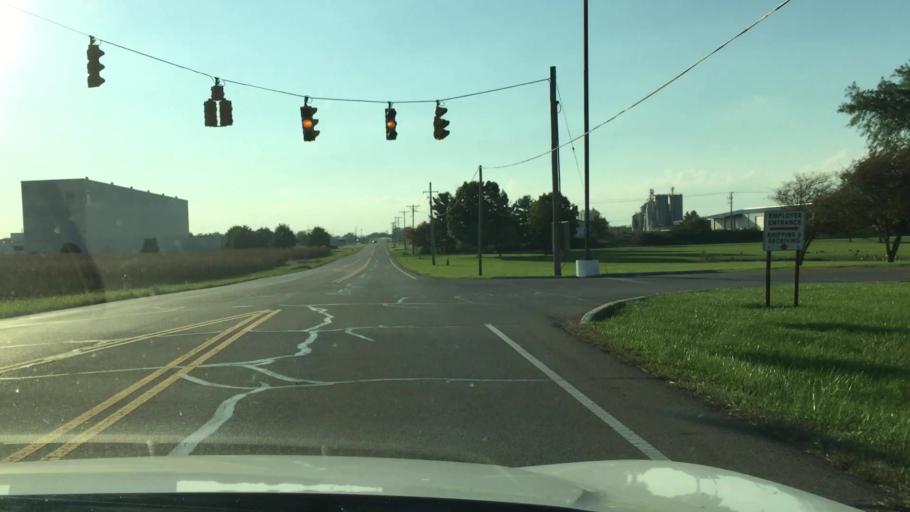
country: US
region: Ohio
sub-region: Champaign County
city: Urbana
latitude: 40.0905
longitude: -83.7658
